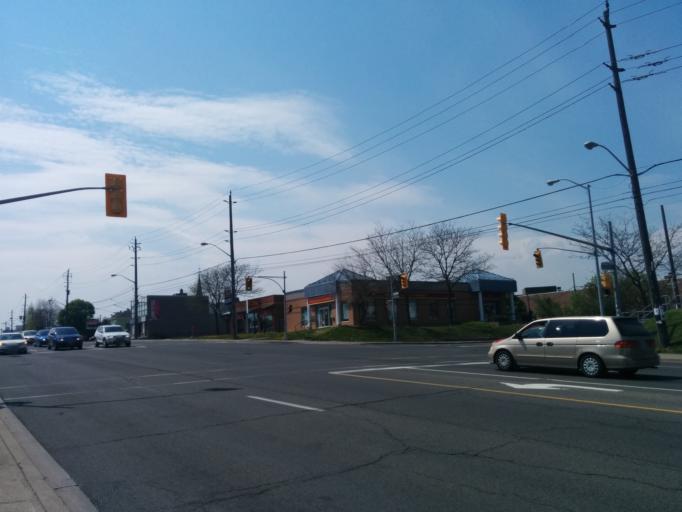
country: CA
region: Ontario
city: Scarborough
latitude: 43.7859
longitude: -79.2756
